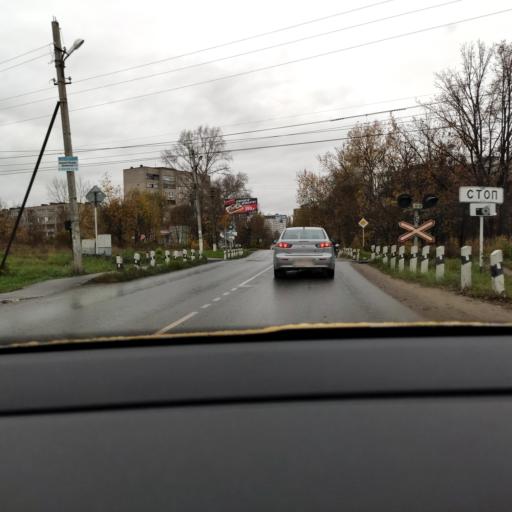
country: RU
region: Moskovskaya
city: Ivanteyevka
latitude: 55.9612
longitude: 37.9216
